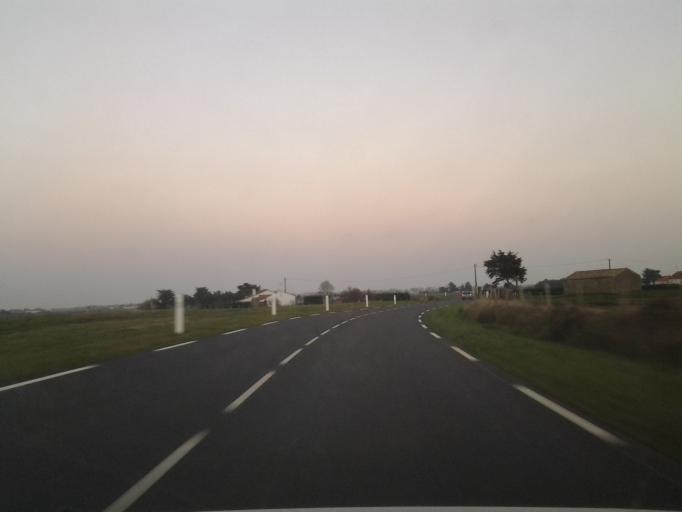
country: FR
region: Pays de la Loire
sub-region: Departement de la Vendee
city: Beauvoir-sur-Mer
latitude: 46.9167
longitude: -2.0731
